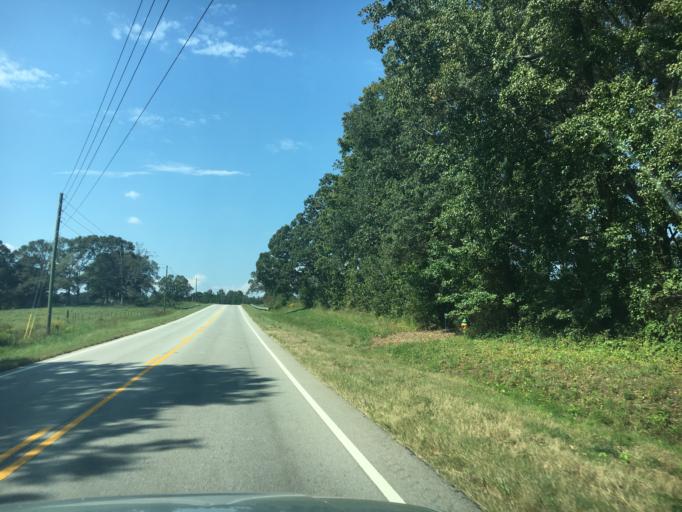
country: US
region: Georgia
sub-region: Franklin County
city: Gumlog
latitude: 34.4601
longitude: -83.0547
